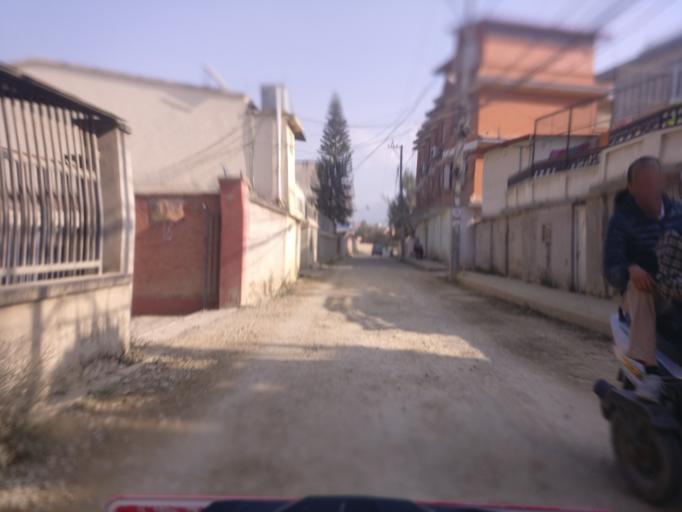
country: NP
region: Central Region
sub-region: Bagmati Zone
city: Patan
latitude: 27.6809
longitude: 85.3208
